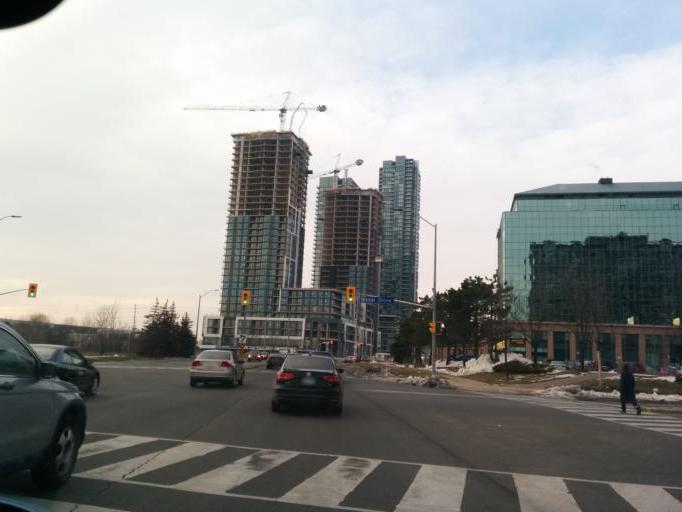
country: CA
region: Ontario
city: Mississauga
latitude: 43.5843
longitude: -79.6427
